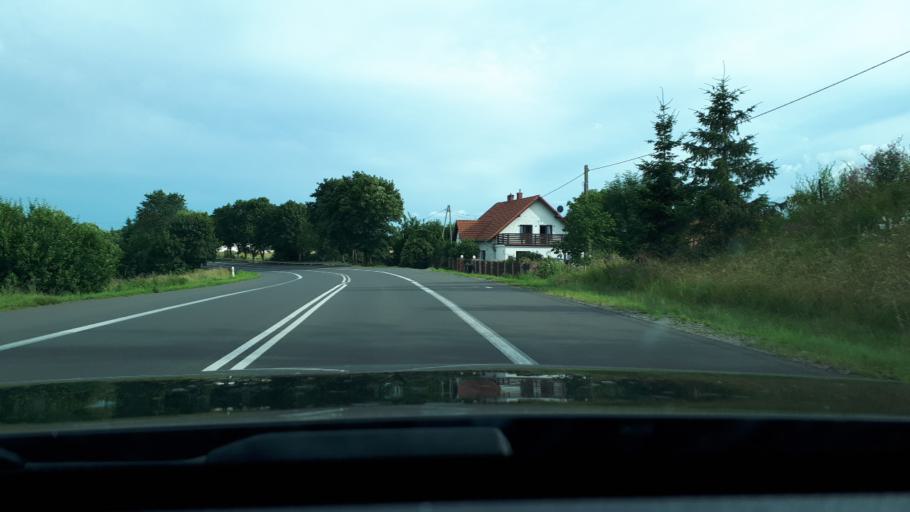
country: PL
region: Warmian-Masurian Voivodeship
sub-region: Powiat ostrodzki
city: Ostroda
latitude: 53.6656
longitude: 20.0393
